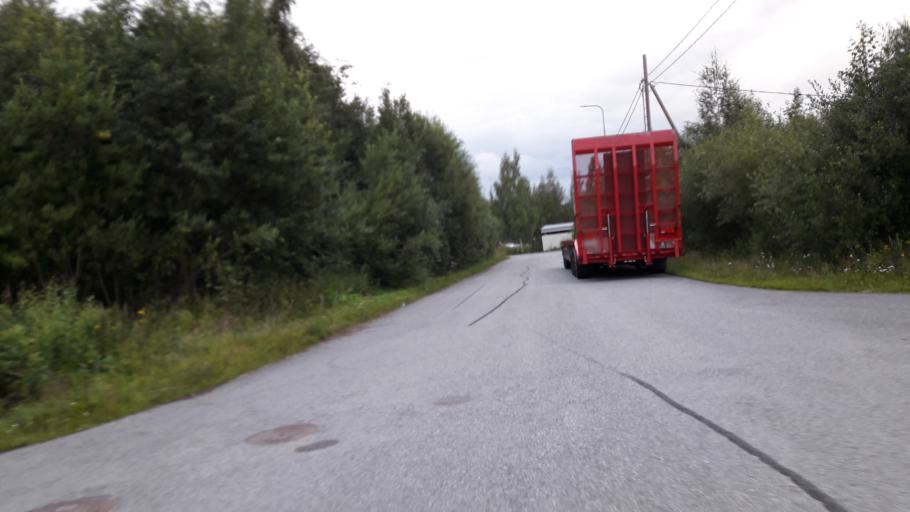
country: FI
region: North Karelia
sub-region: Joensuu
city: Joensuu
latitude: 62.5508
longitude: 29.8361
